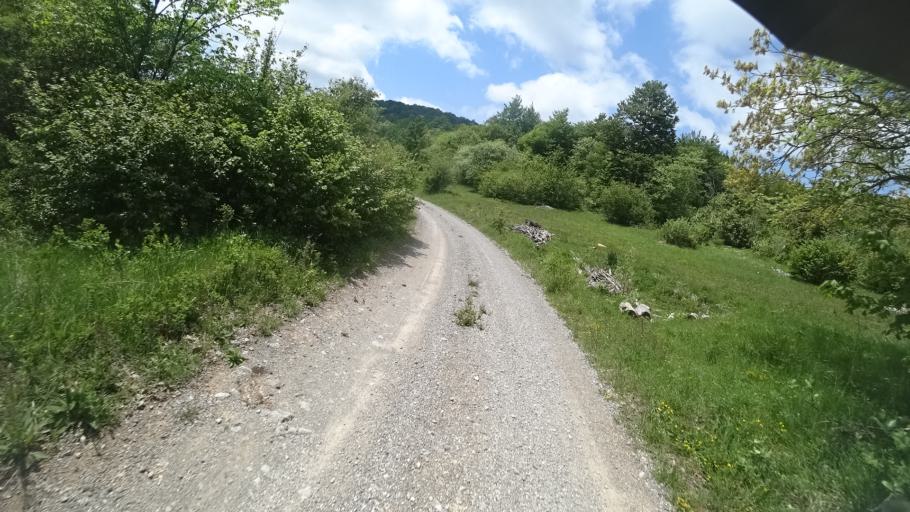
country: HR
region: Zadarska
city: Gracac
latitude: 44.5058
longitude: 15.8820
